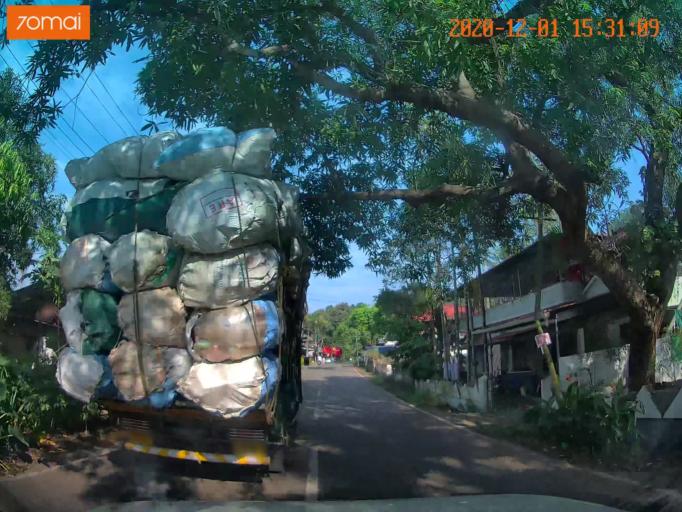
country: IN
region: Kerala
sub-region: Ernakulam
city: Muvattupuzha
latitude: 9.9685
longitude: 76.5679
